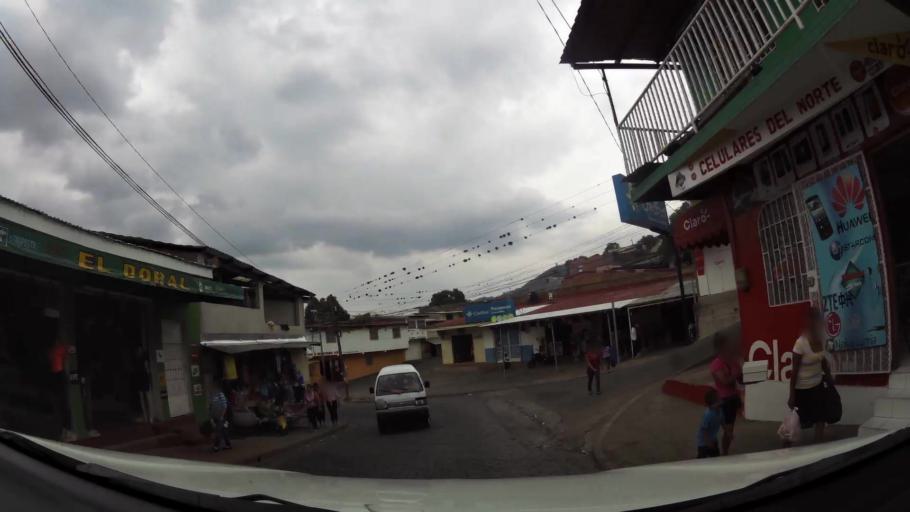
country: NI
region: Matagalpa
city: Matagalpa
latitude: 12.9313
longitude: -85.9138
